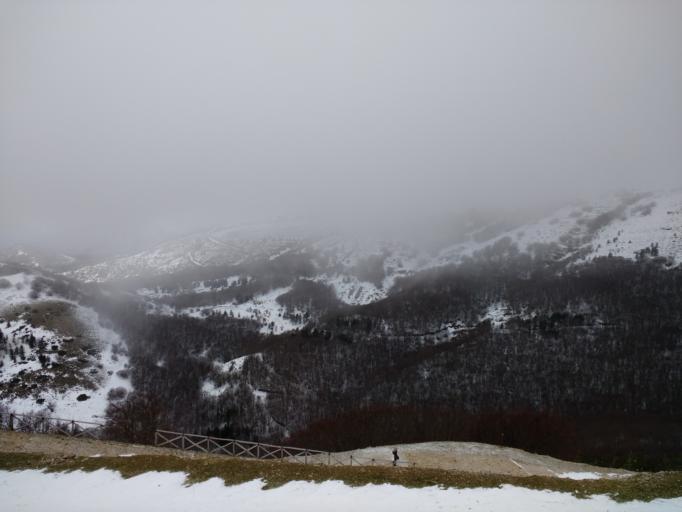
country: IT
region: Sicily
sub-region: Palermo
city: Castellana Sicula
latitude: 37.8321
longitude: 14.0507
